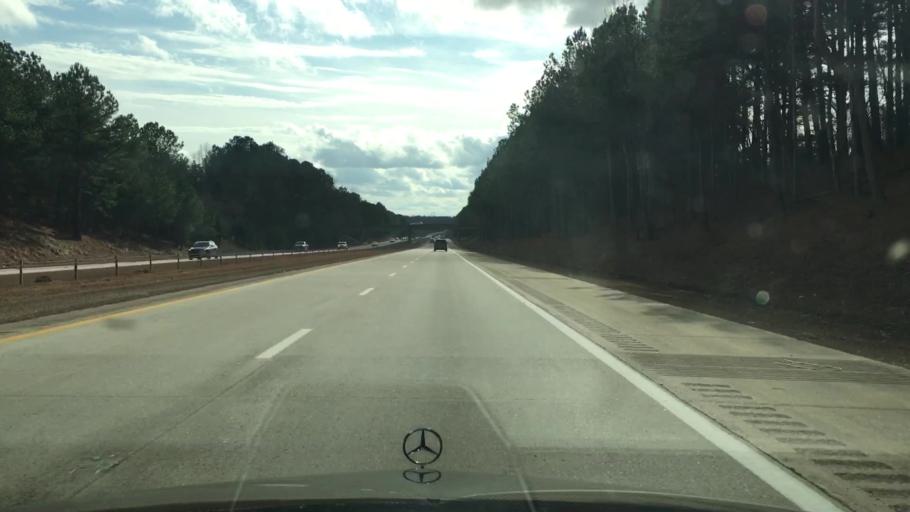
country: US
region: North Carolina
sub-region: Wake County
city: Garner
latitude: 35.5770
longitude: -78.5766
